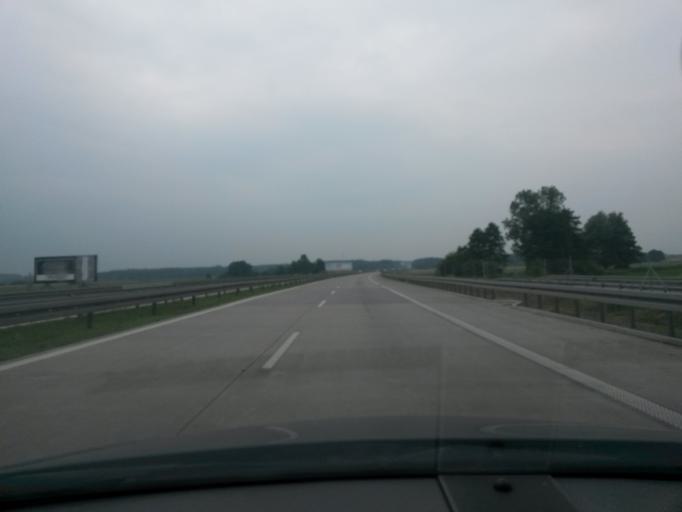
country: PL
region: Lodz Voivodeship
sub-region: Powiat piotrkowski
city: Wolborz
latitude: 51.5008
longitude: 19.8628
